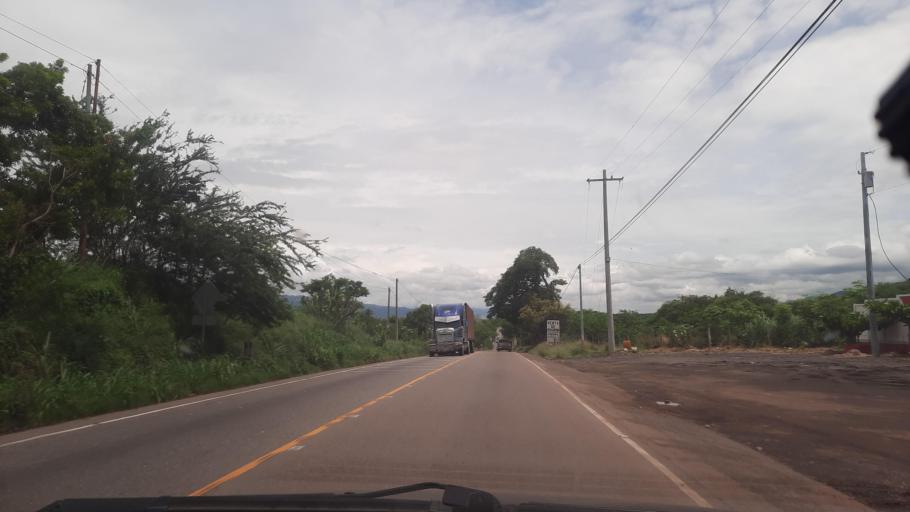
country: GT
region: Zacapa
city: Rio Hondo
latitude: 15.0493
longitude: -89.5670
